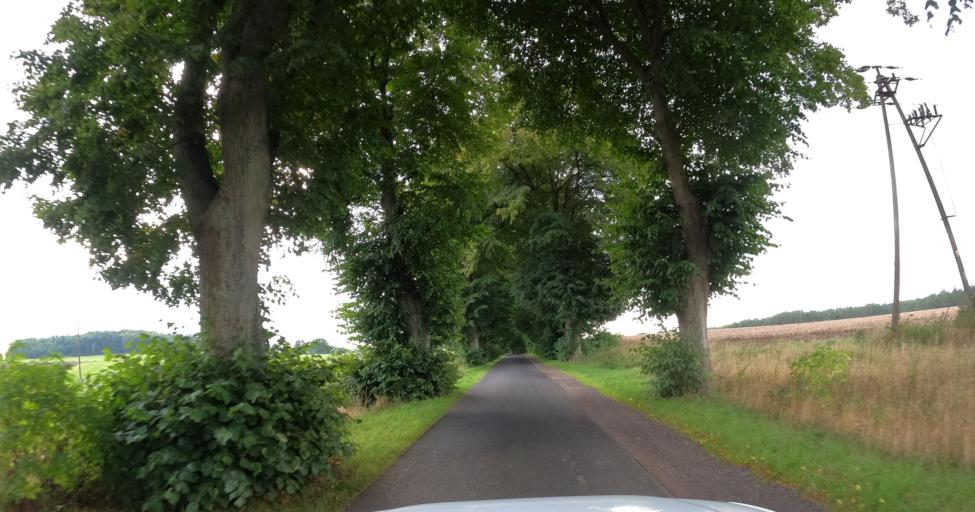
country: PL
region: West Pomeranian Voivodeship
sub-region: Powiat kolobrzeski
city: Ryman
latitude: 53.9699
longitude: 15.4677
